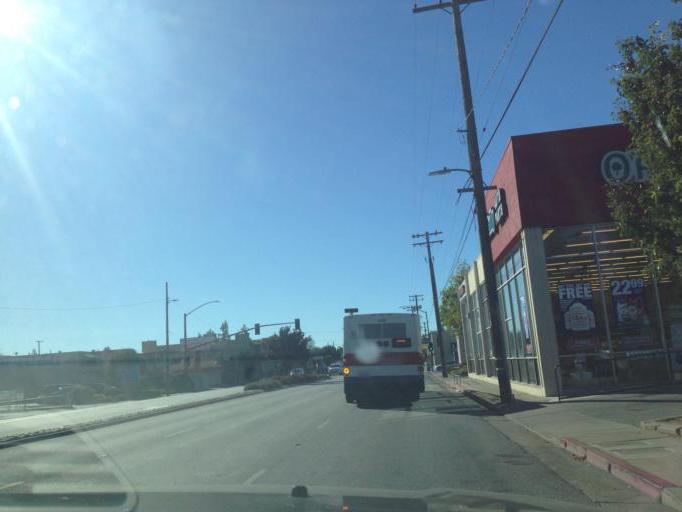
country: US
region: California
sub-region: San Mateo County
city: Redwood City
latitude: 37.4742
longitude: -122.2185
